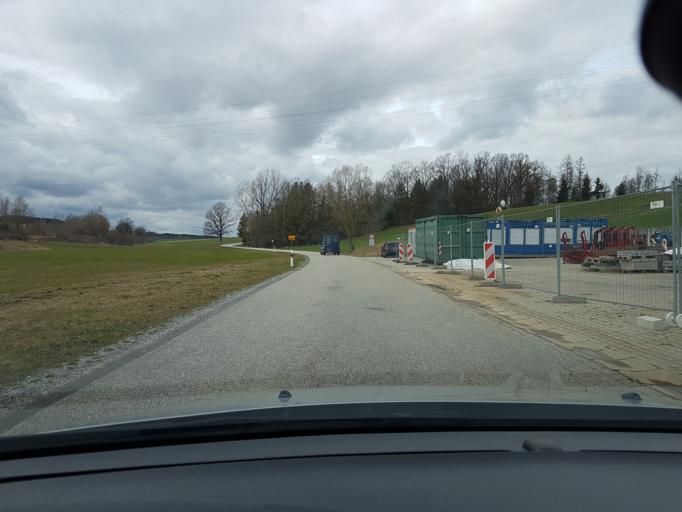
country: DE
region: Bavaria
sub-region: Lower Bavaria
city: Vilsbiburg
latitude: 48.4592
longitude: 12.3410
